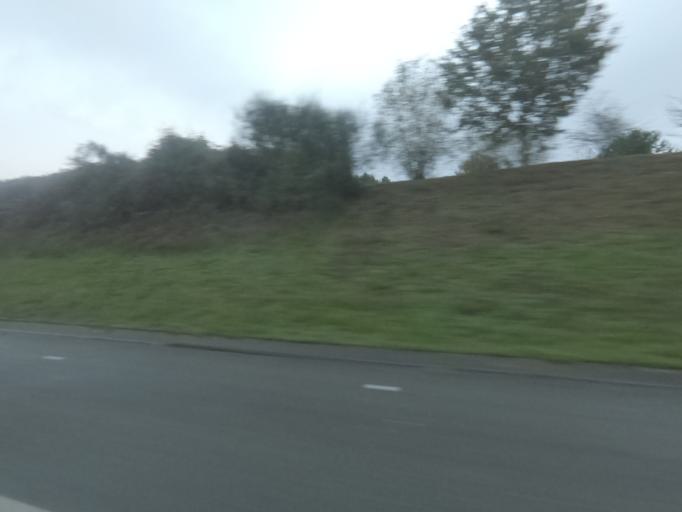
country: PT
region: Braga
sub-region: Barcelos
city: Galegos
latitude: 41.6158
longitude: -8.5519
